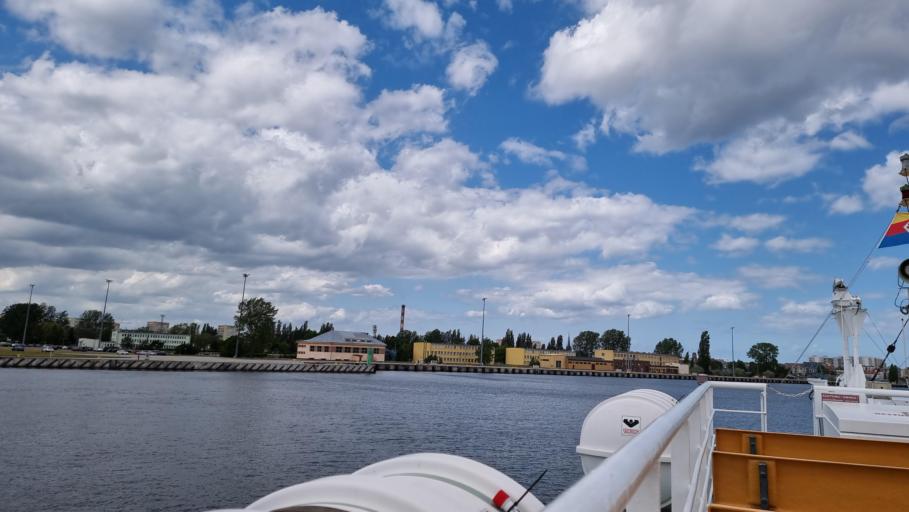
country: PL
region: West Pomeranian Voivodeship
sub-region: Swinoujscie
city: Swinoujscie
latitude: 53.8983
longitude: 14.2536
